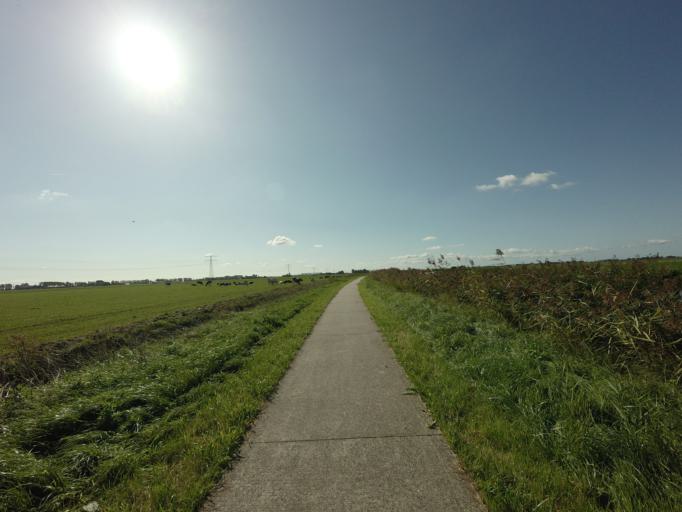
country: NL
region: Friesland
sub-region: Gemeente Boarnsterhim
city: Reduzum
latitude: 53.1443
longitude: 5.7644
